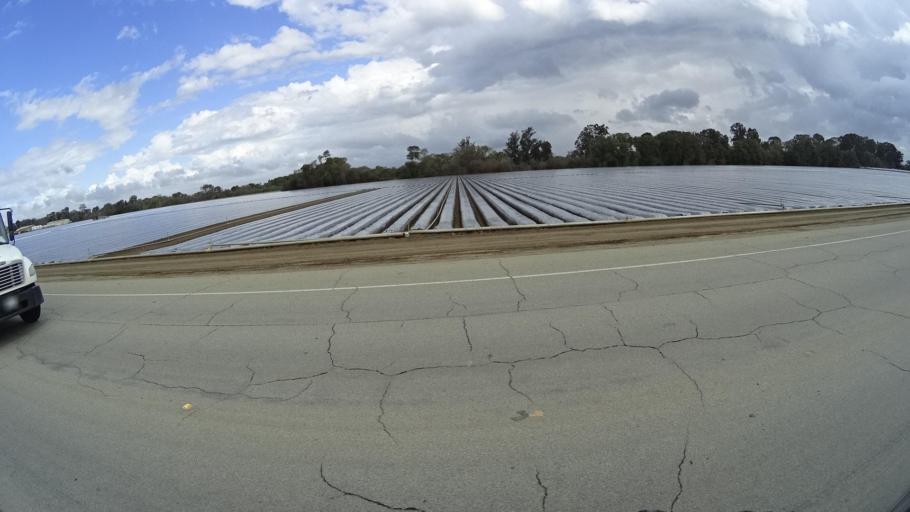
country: US
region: California
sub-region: Monterey County
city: Salinas
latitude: 36.6351
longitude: -121.7019
